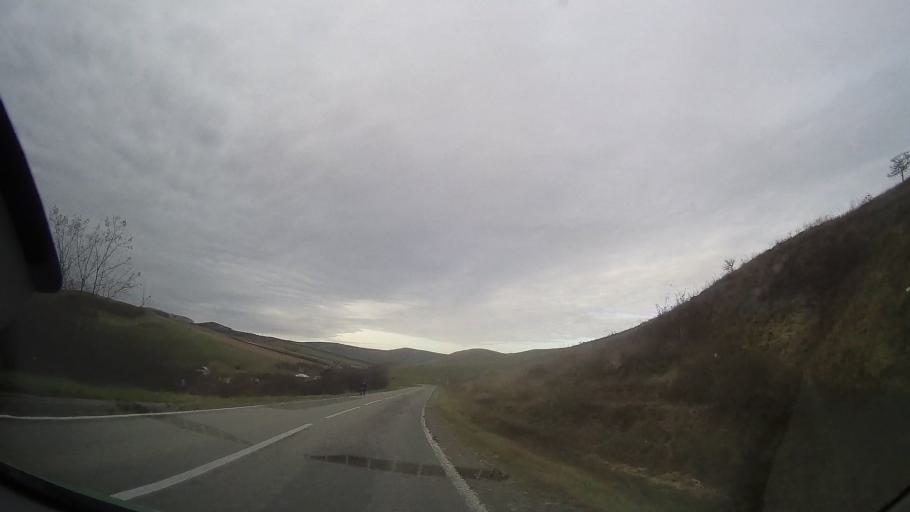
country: RO
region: Mures
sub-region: Comuna Sarmasu
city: Sarmasu
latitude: 46.7950
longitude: 24.1822
